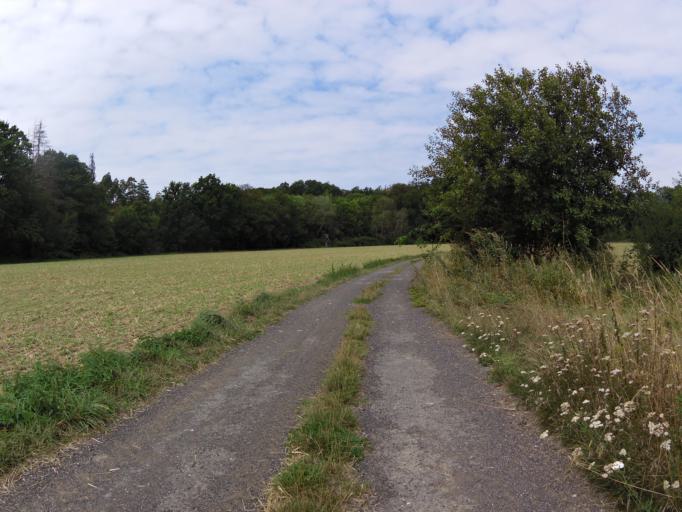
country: DE
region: Bavaria
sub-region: Regierungsbezirk Unterfranken
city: Kleinrinderfeld
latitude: 49.7063
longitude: 9.8258
